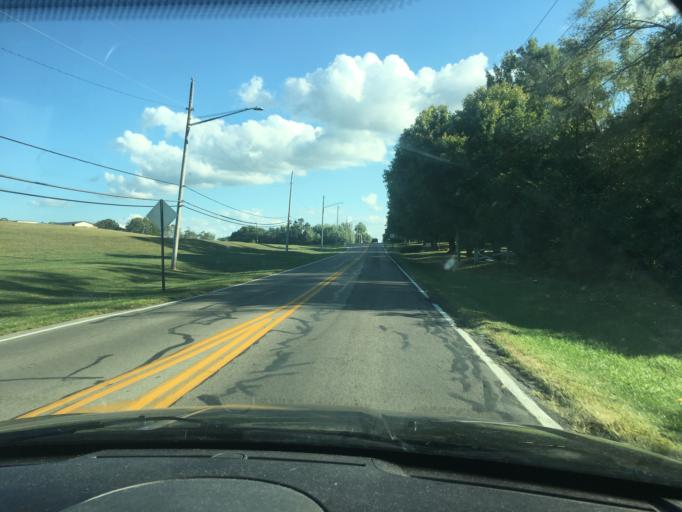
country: US
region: Ohio
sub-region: Logan County
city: Bellefontaine
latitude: 40.3456
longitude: -83.7485
